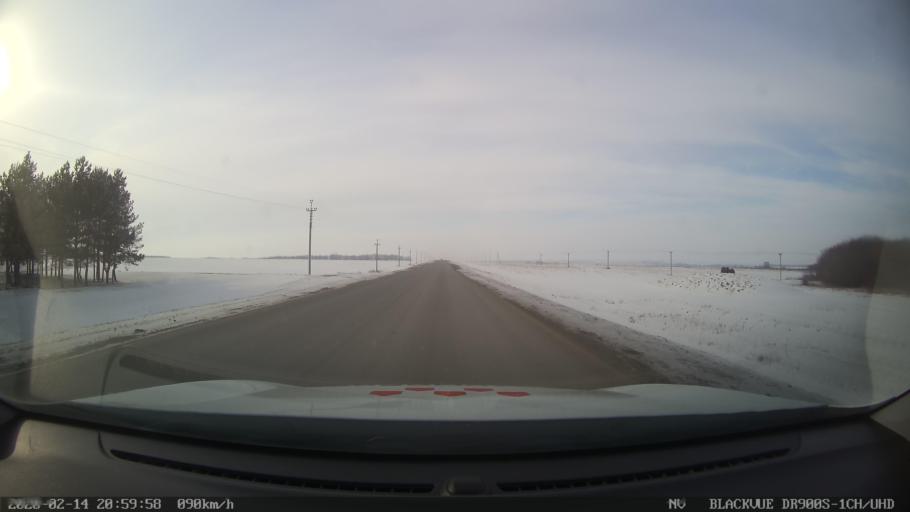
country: RU
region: Tatarstan
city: Kuybyshevskiy Zaton
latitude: 55.1746
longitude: 49.2294
